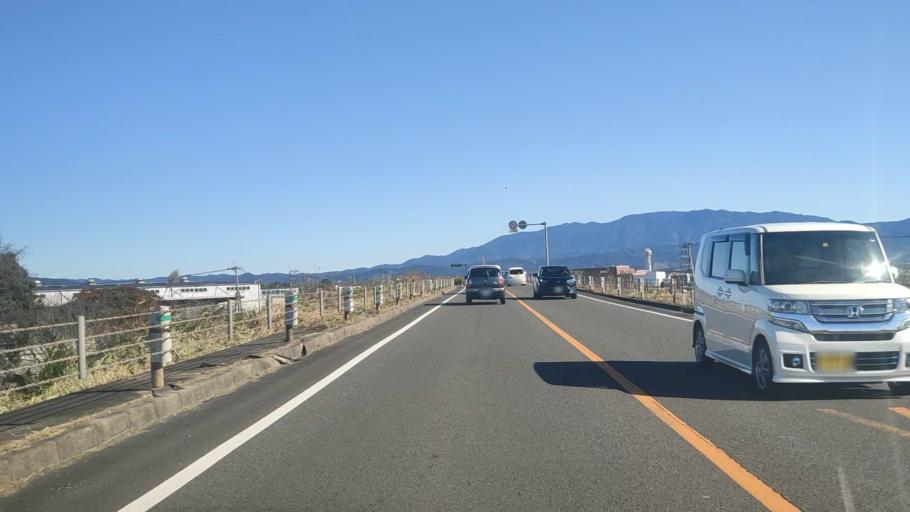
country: JP
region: Miyazaki
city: Miyakonojo
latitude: 31.7793
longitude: 131.1052
